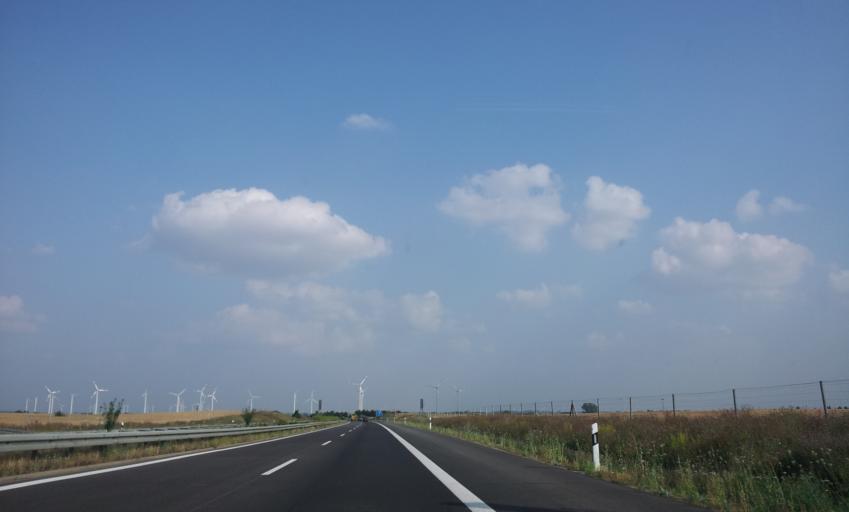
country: DE
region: Mecklenburg-Vorpommern
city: Strasburg
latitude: 53.5247
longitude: 13.7689
